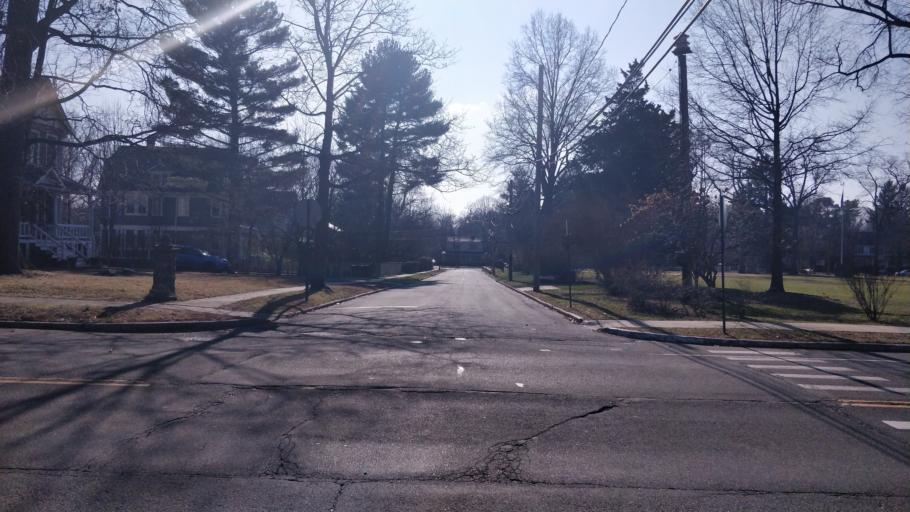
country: US
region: New York
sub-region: Nassau County
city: Sea Cliff
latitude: 40.8500
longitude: -73.6386
